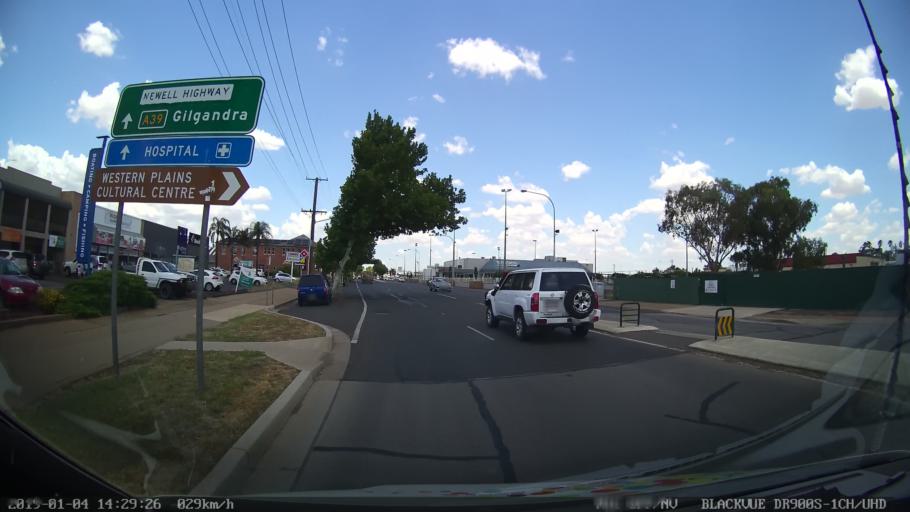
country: AU
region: New South Wales
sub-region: Dubbo Municipality
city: Dubbo
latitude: -32.2433
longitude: 148.6072
